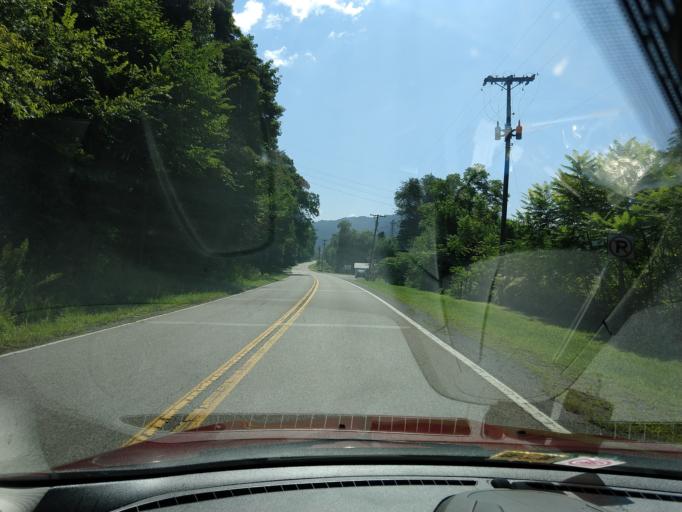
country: US
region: West Virginia
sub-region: Kanawha County
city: Montgomery
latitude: 38.1384
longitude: -81.2755
